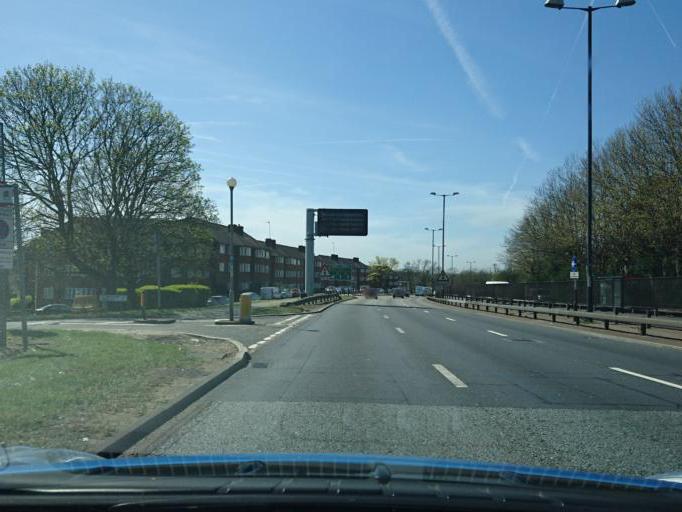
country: GB
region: England
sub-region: Greater London
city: Hendon
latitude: 51.5903
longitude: -0.1921
